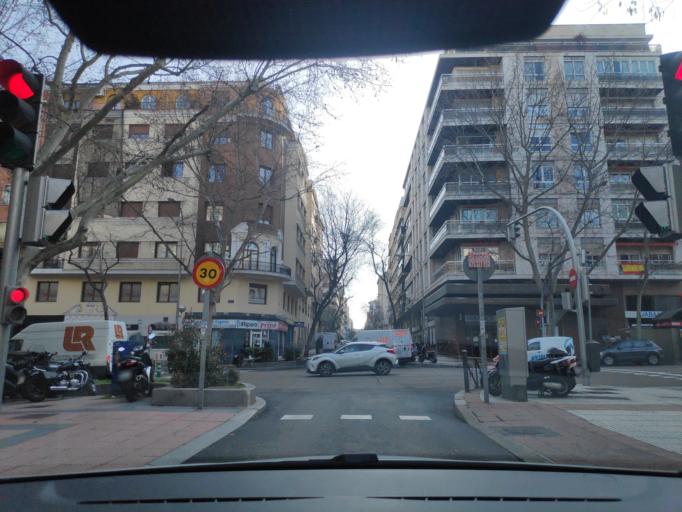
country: ES
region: Madrid
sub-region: Provincia de Madrid
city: Salamanca
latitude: 40.4362
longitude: -3.6835
